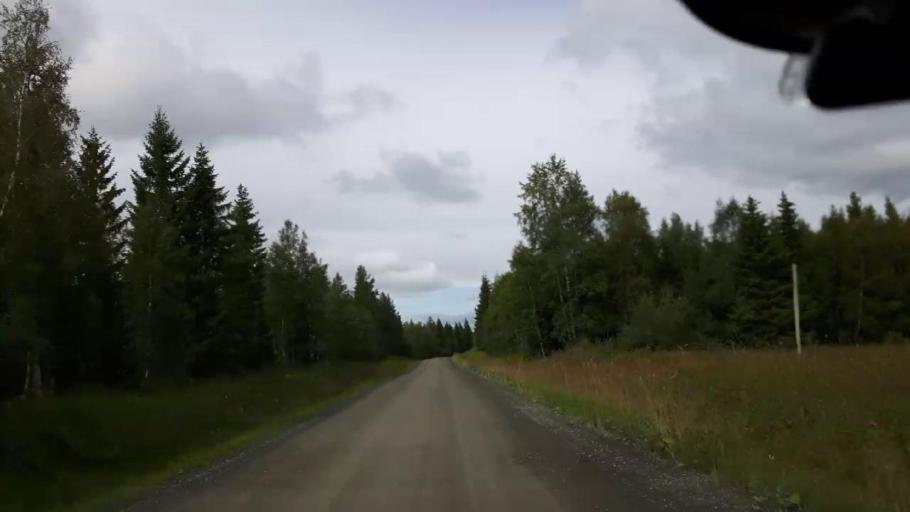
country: SE
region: Jaemtland
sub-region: Krokoms Kommun
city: Krokom
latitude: 63.3893
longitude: 14.1093
